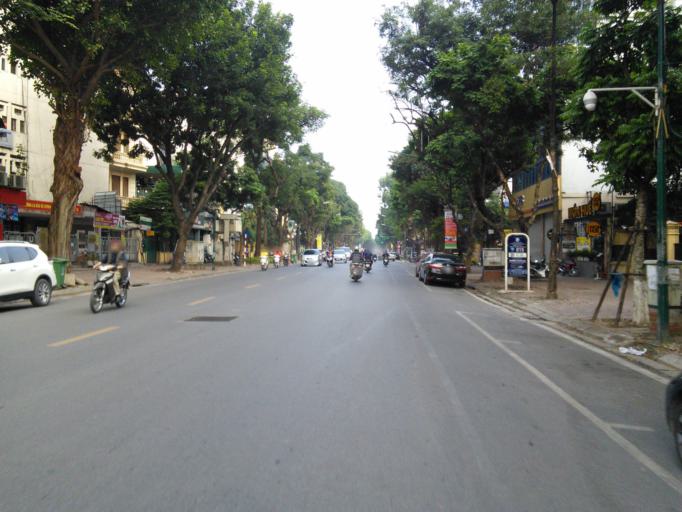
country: VN
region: Ha Noi
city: Hanoi
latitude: 21.0224
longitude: 105.8471
